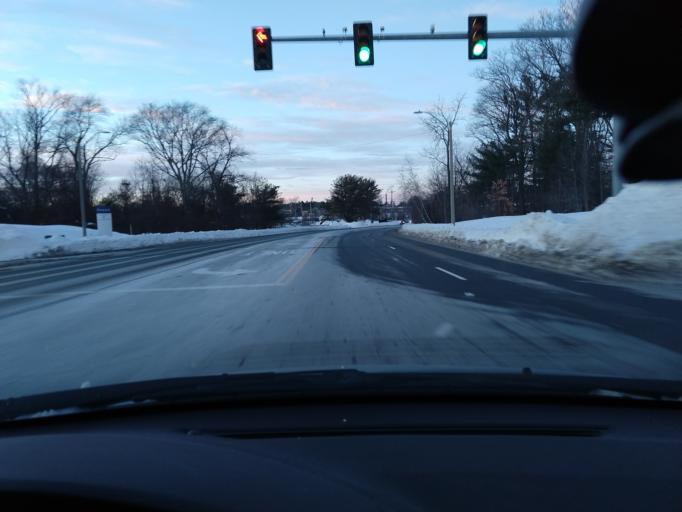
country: US
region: Massachusetts
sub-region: Middlesex County
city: Pinehurst
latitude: 42.5000
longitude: -71.2334
